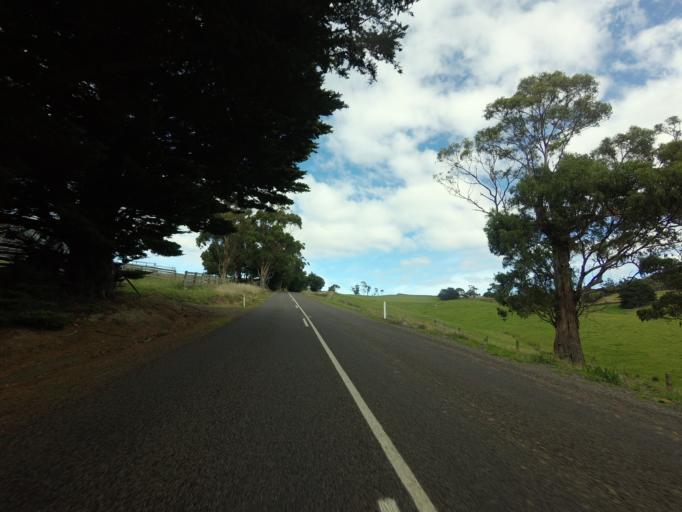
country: AU
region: Tasmania
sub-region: Clarence
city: Sandford
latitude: -43.0641
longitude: 147.7493
